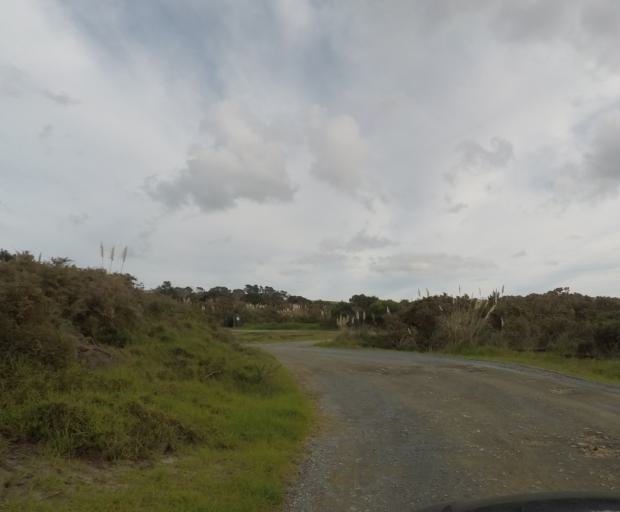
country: NZ
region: Northland
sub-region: Whangarei
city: Ruakaka
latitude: -35.9318
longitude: 174.4594
